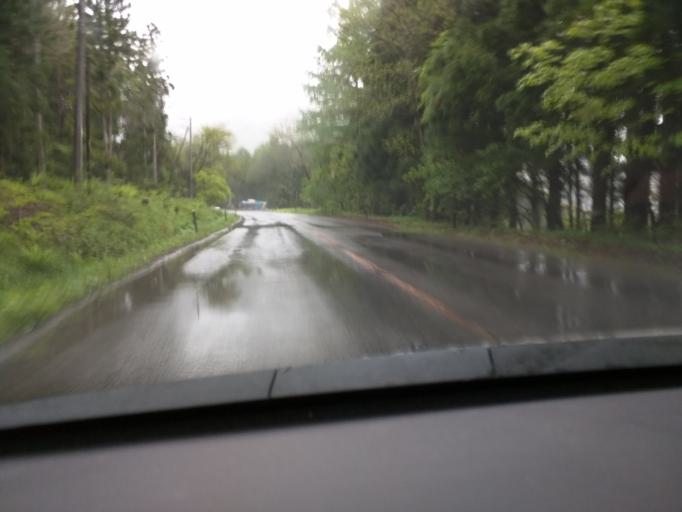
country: JP
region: Fukushima
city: Inawashiro
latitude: 37.6015
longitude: 140.1250
